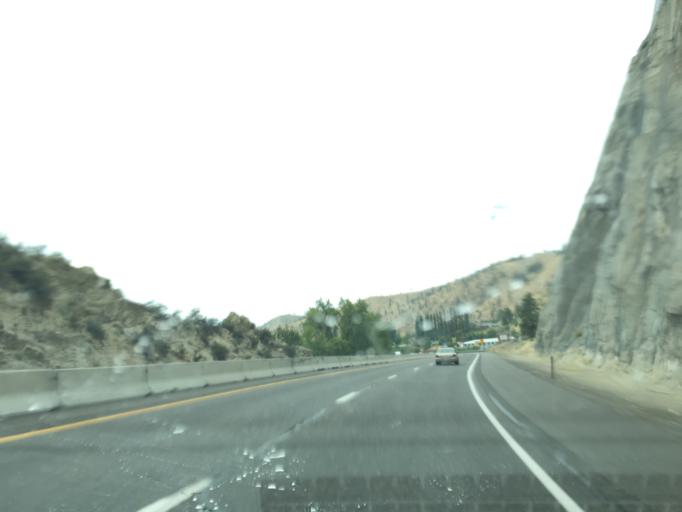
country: US
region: Washington
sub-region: Chelan County
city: Cashmere
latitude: 47.5254
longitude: -120.4823
